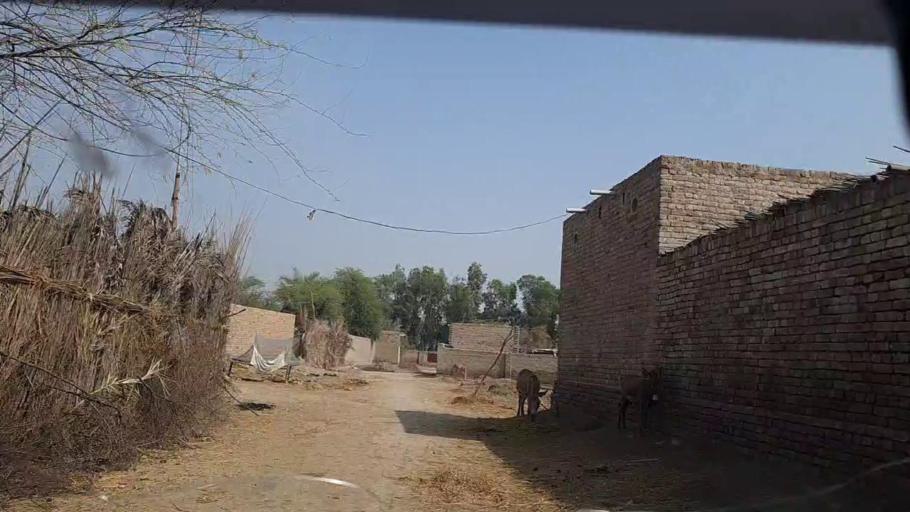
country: PK
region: Sindh
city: Shikarpur
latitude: 28.0924
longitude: 68.6696
